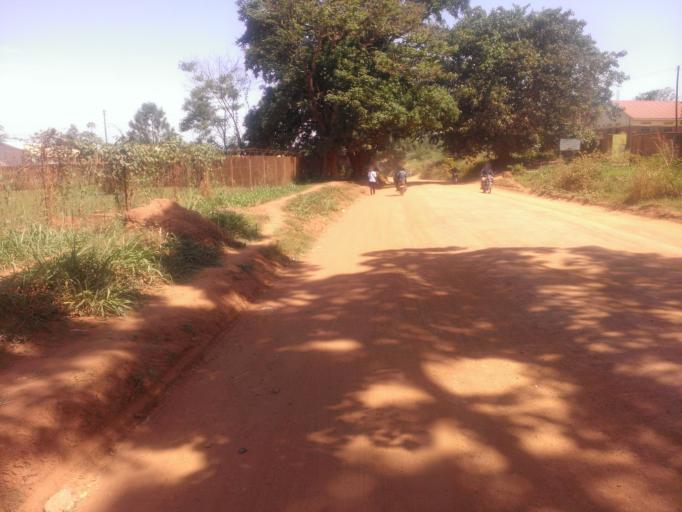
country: UG
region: Northern Region
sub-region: Gulu District
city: Gulu
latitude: 2.7807
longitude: 32.2948
